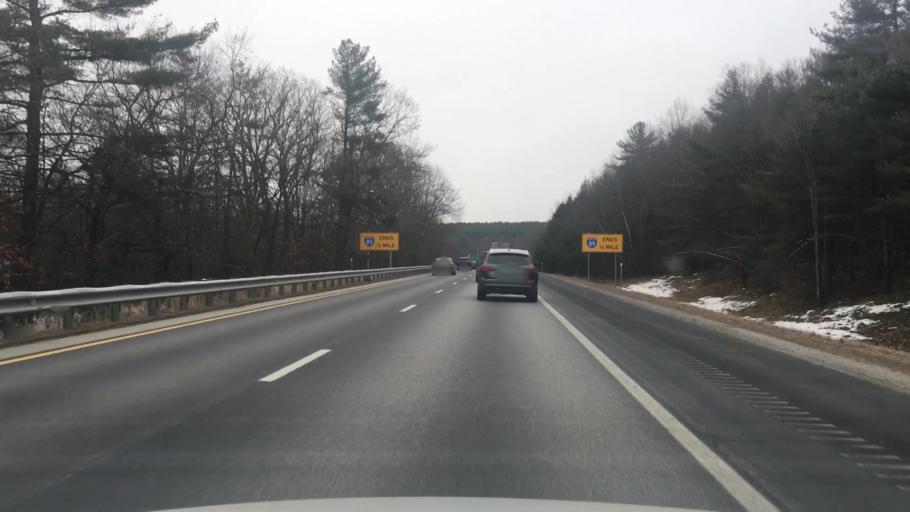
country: US
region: New Hampshire
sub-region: Merrimack County
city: Concord
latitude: 43.1700
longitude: -71.5450
